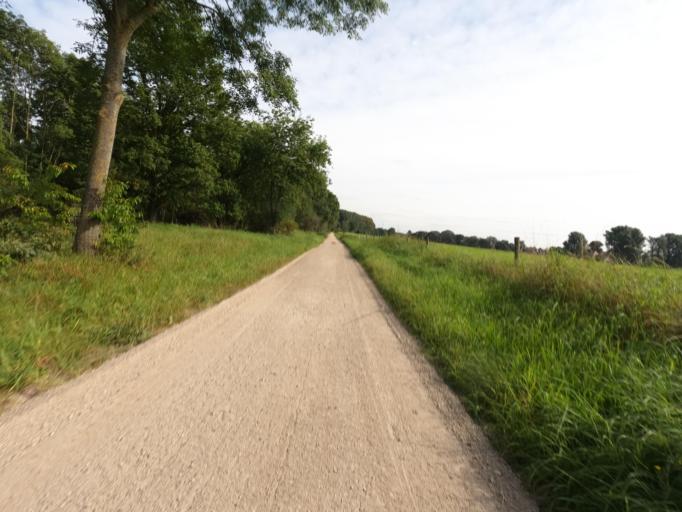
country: DE
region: North Rhine-Westphalia
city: Huckelhoven
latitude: 51.0252
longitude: 6.2451
